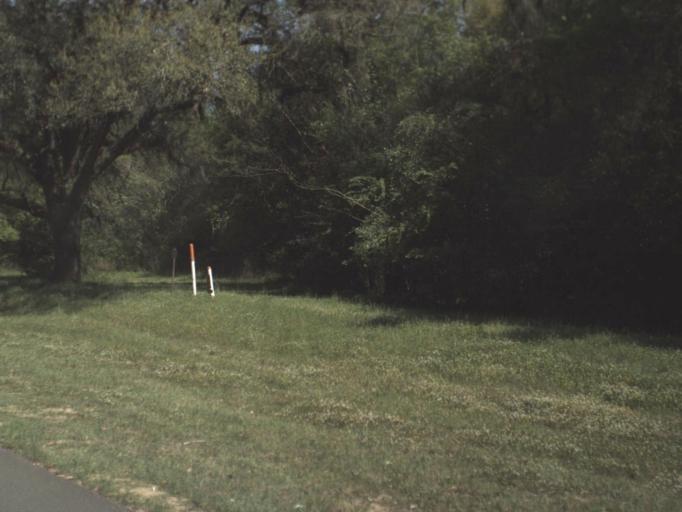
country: US
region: Florida
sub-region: Okaloosa County
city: Crestview
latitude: 30.7526
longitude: -86.6321
